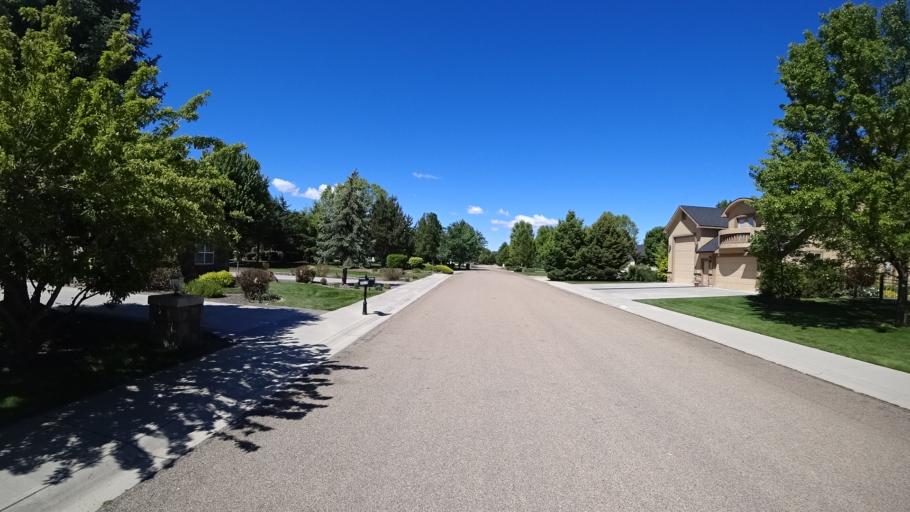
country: US
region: Idaho
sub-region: Ada County
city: Eagle
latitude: 43.6673
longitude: -116.3839
